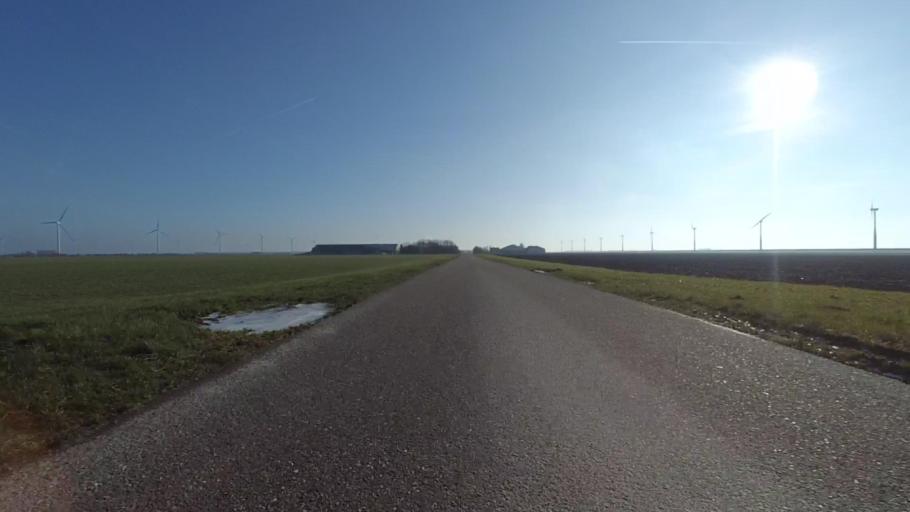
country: NL
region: Utrecht
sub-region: Gemeente Bunschoten
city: Spakenburg
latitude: 52.2898
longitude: 5.3558
